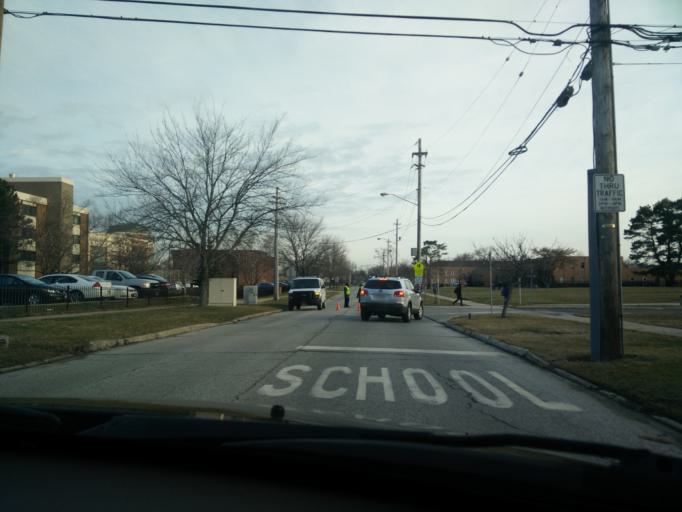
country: US
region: Ohio
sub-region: Cuyahoga County
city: University Heights
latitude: 41.4990
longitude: -81.5313
